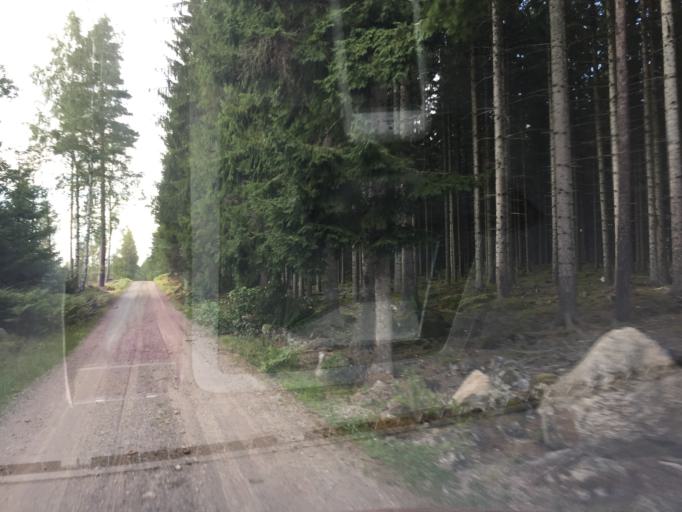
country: SE
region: Soedermanland
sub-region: Vingakers Kommun
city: Vingaker
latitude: 58.9895
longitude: 15.6908
